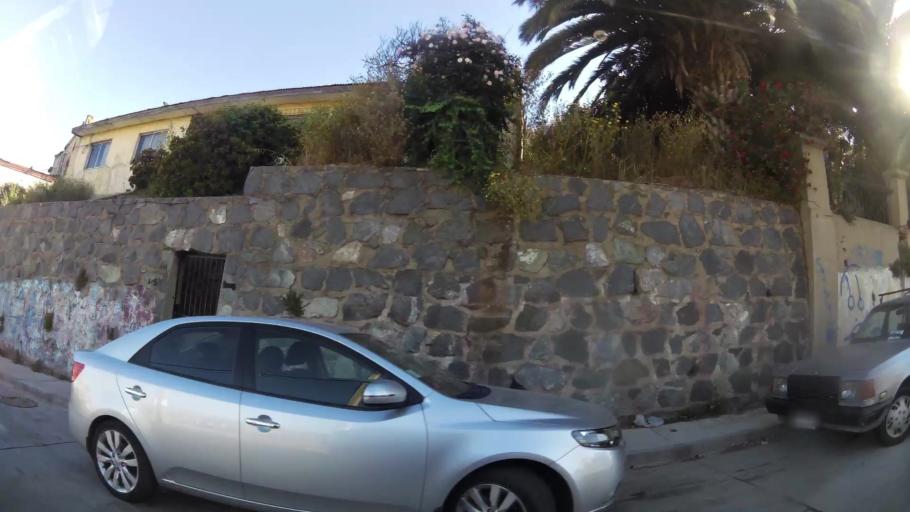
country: CL
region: Valparaiso
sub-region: Provincia de Valparaiso
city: Valparaiso
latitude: -33.0508
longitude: -71.6170
